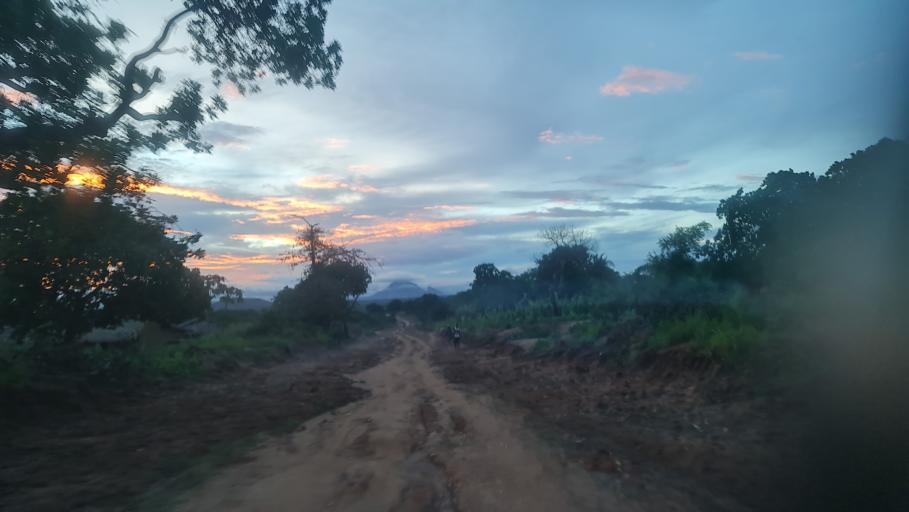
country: MZ
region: Nampula
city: Nampula
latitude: -14.7340
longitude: 39.9172
